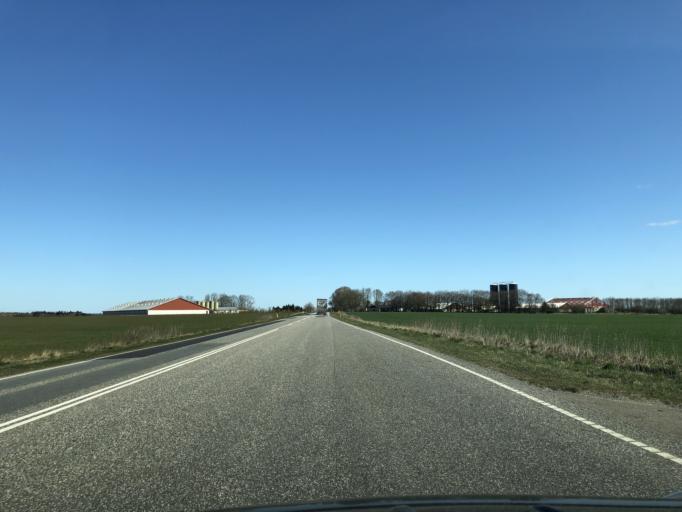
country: DK
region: North Denmark
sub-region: Rebild Kommune
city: Stovring
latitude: 56.8525
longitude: 9.8235
